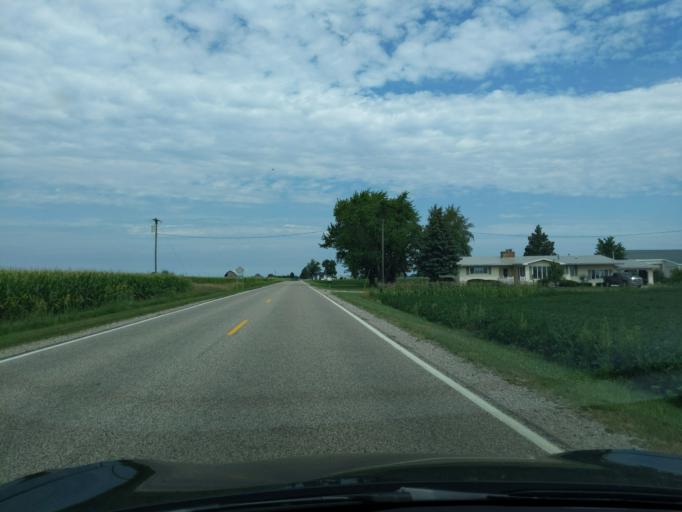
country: US
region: Michigan
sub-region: Gratiot County
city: Breckenridge
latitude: 43.3367
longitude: -84.4296
